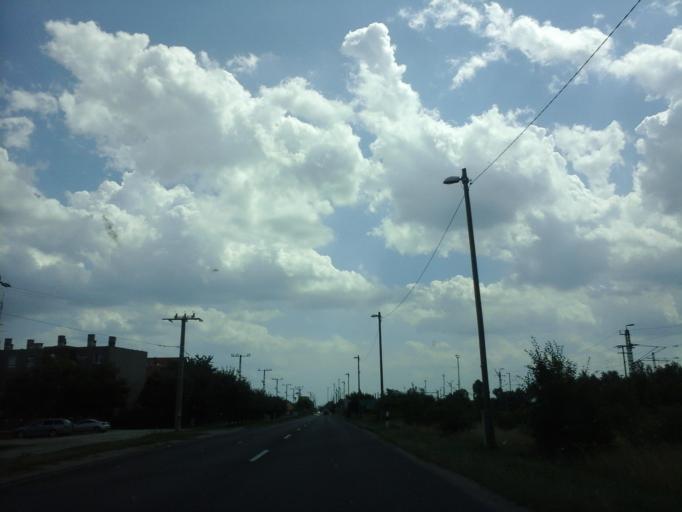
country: HU
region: Gyor-Moson-Sopron
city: Rajka
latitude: 48.0023
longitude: 17.1876
